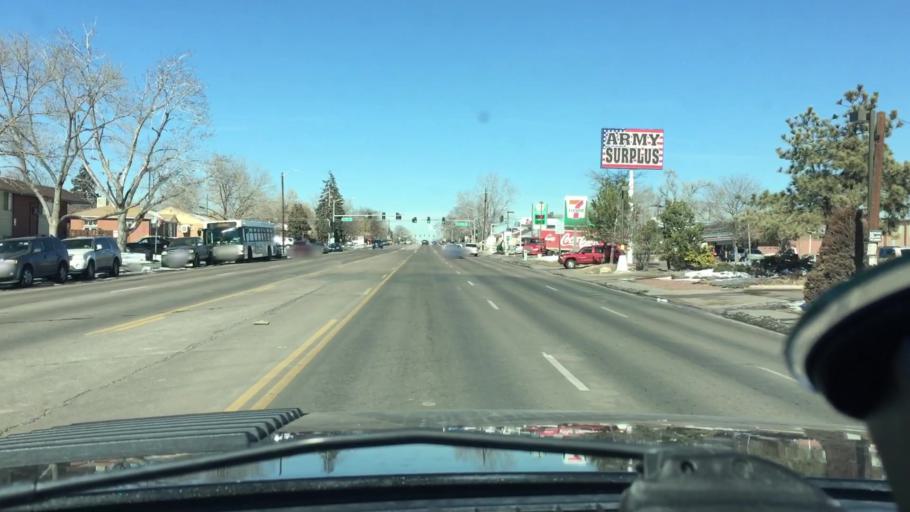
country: US
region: Colorado
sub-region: Adams County
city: Sherrelwood
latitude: 39.8330
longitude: -105.0060
